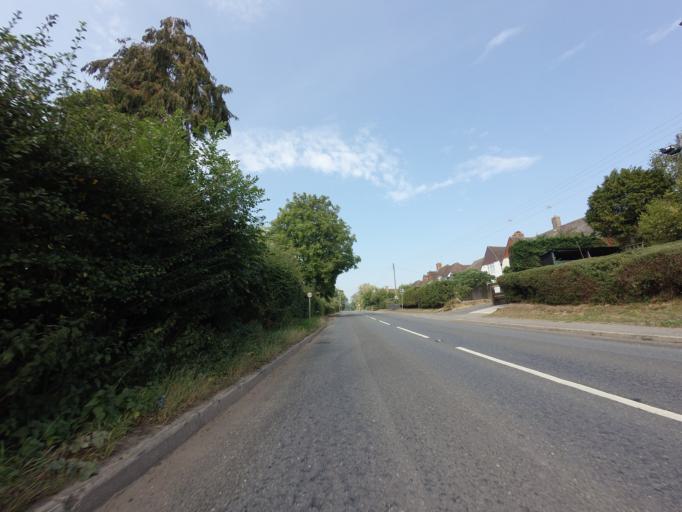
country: GB
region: England
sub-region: Kent
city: Headcorn
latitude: 51.1146
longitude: 0.6368
